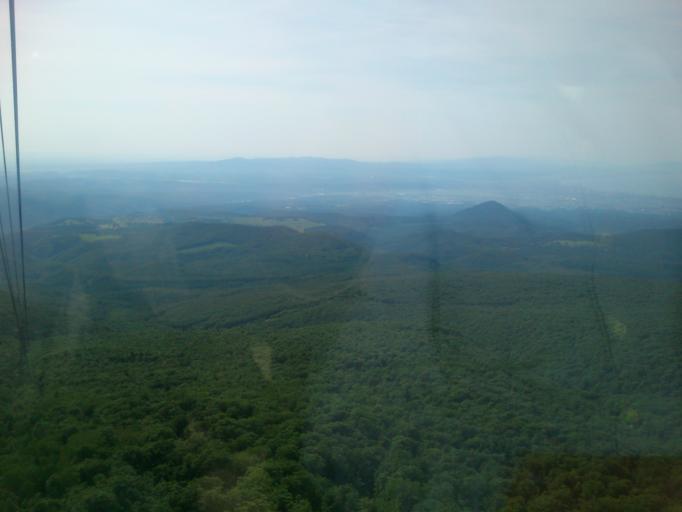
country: JP
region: Aomori
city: Aomori Shi
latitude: 40.6770
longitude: 140.8527
